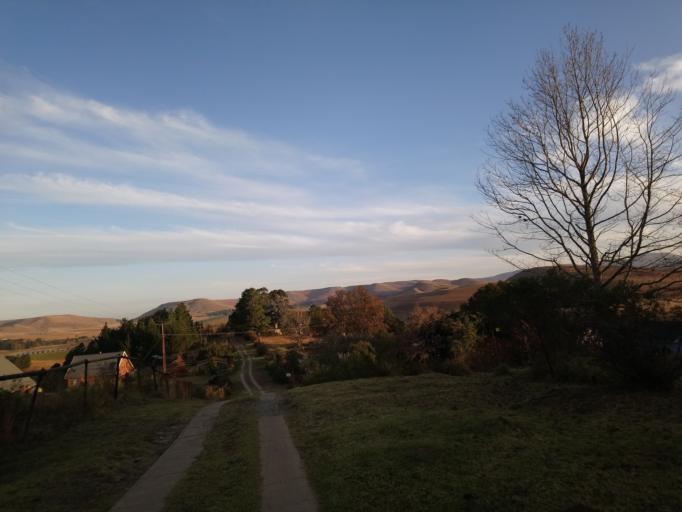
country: ZA
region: KwaZulu-Natal
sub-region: uMgungundlovu District Municipality
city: Mooirivier
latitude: -29.3310
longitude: 29.9193
